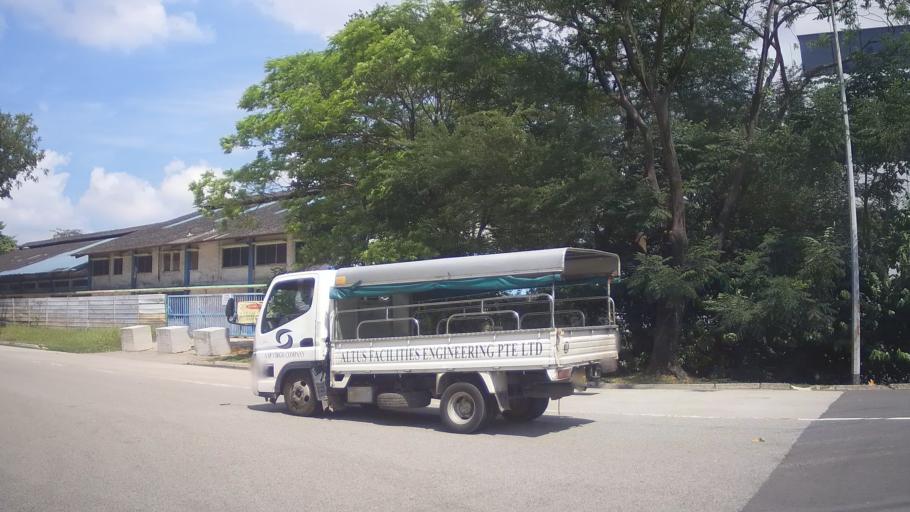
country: SG
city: Singapore
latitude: 1.3265
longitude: 103.7148
